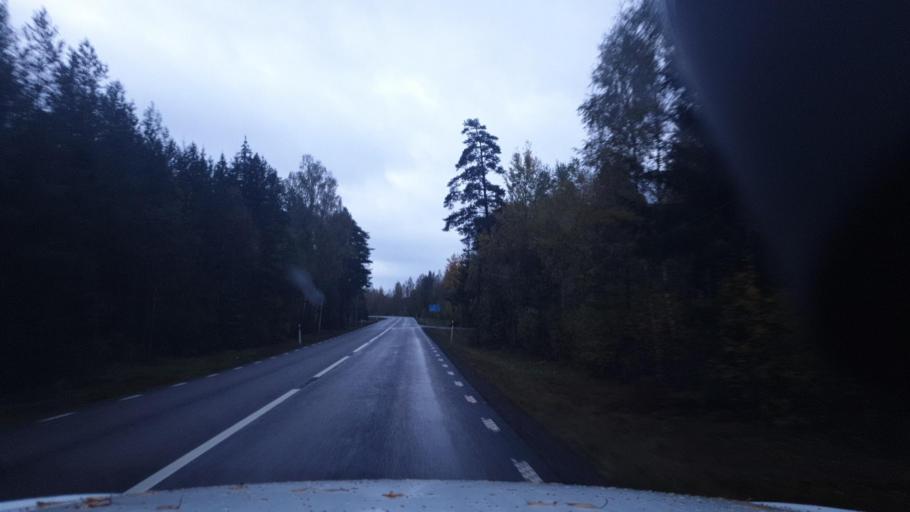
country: SE
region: Vaermland
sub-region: Eda Kommun
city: Charlottenberg
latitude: 59.8473
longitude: 12.3110
